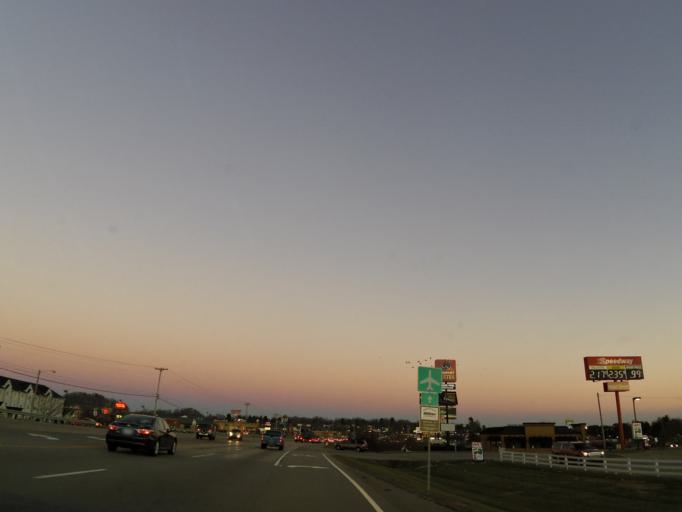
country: US
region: Kentucky
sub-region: Laurel County
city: London
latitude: 37.1116
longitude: -84.0970
